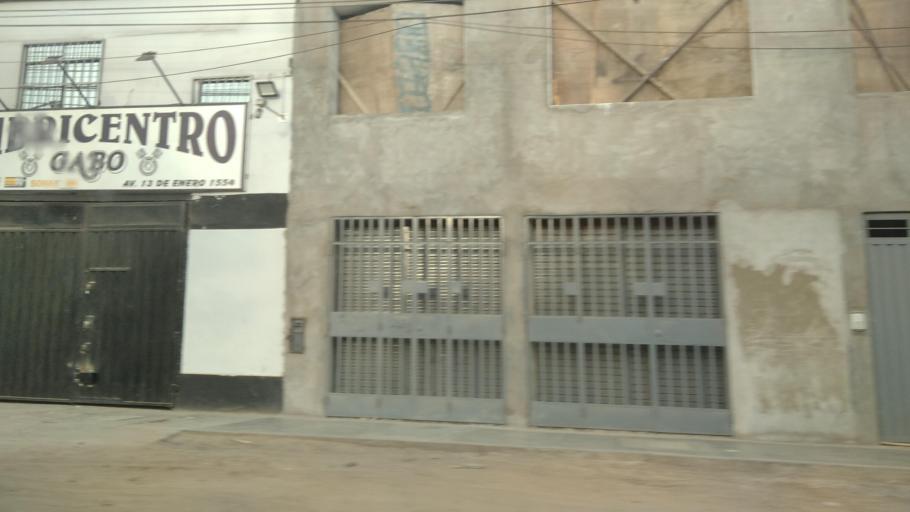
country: PE
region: Lima
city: Lima
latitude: -12.0070
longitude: -77.0007
